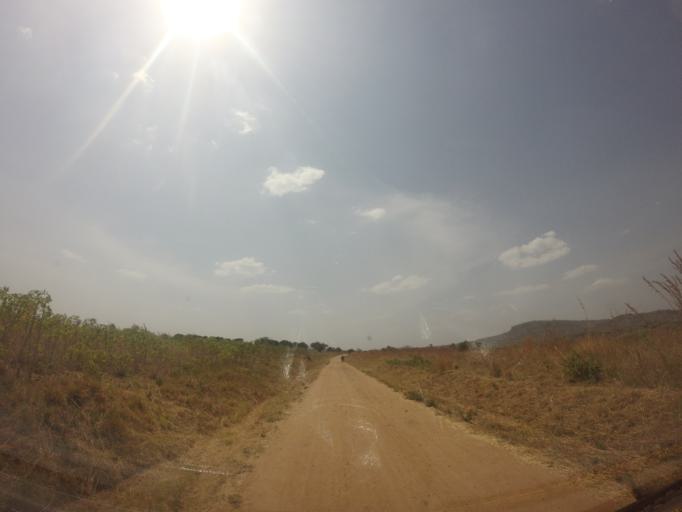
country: UG
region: Northern Region
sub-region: Arua District
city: Arua
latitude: 2.9129
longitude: 31.0425
